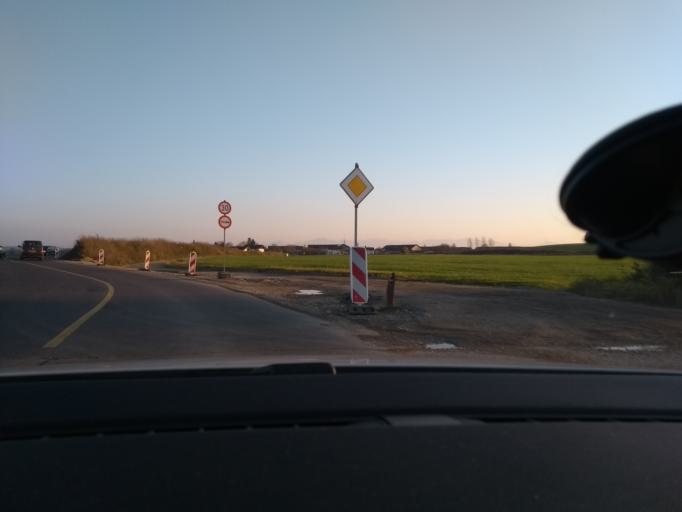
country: DE
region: Bavaria
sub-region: Upper Bavaria
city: Eiselfing
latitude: 48.0366
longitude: 12.2368
